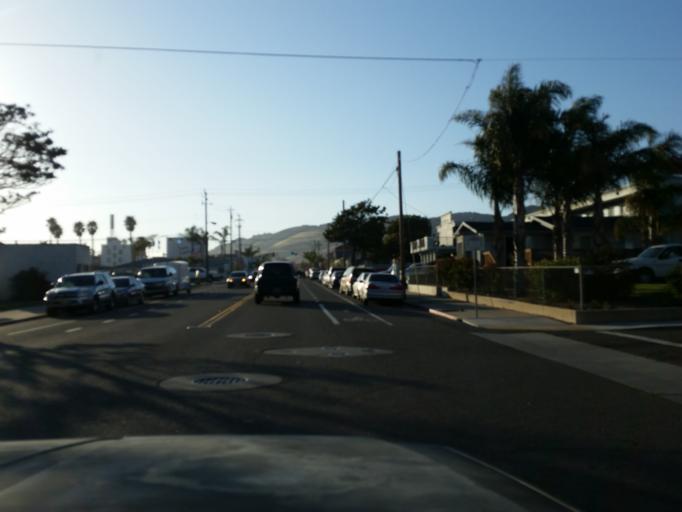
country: US
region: California
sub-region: San Luis Obispo County
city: Pismo Beach
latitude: 35.1386
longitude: -120.6390
